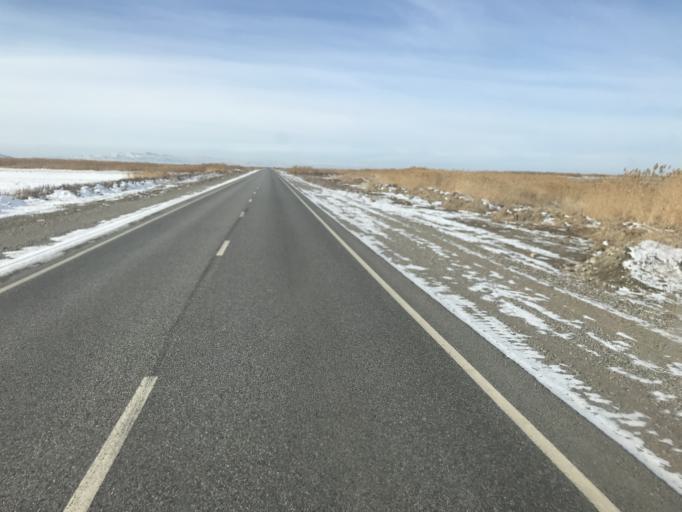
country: KZ
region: Zhambyl
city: Sarykemer
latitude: 43.0337
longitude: 71.3920
